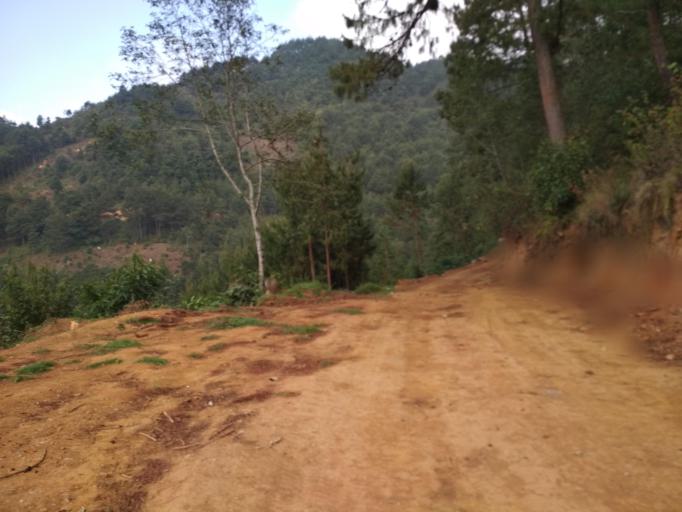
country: MX
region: Veracruz
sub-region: Camerino Z. Mendoza
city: Necoxtla
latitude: 18.7545
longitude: -97.1593
